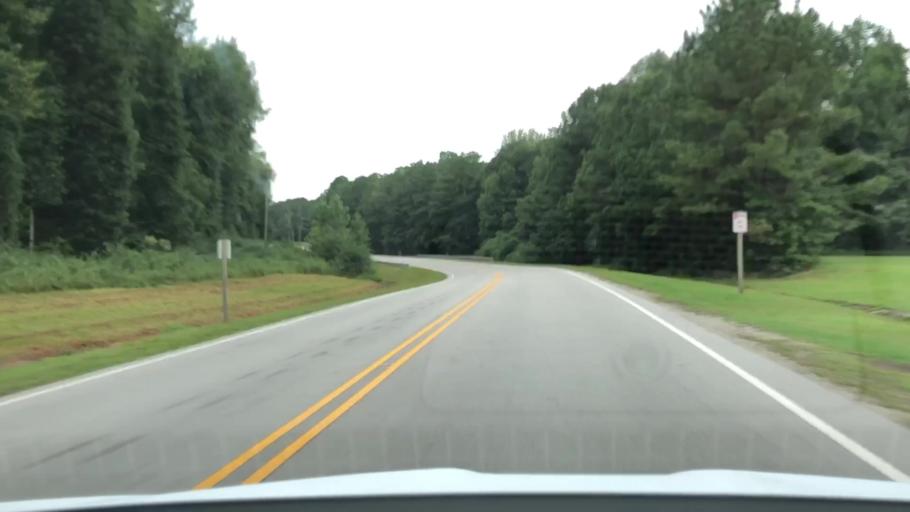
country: US
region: North Carolina
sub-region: Jones County
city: Trenton
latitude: 35.0324
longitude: -77.3171
